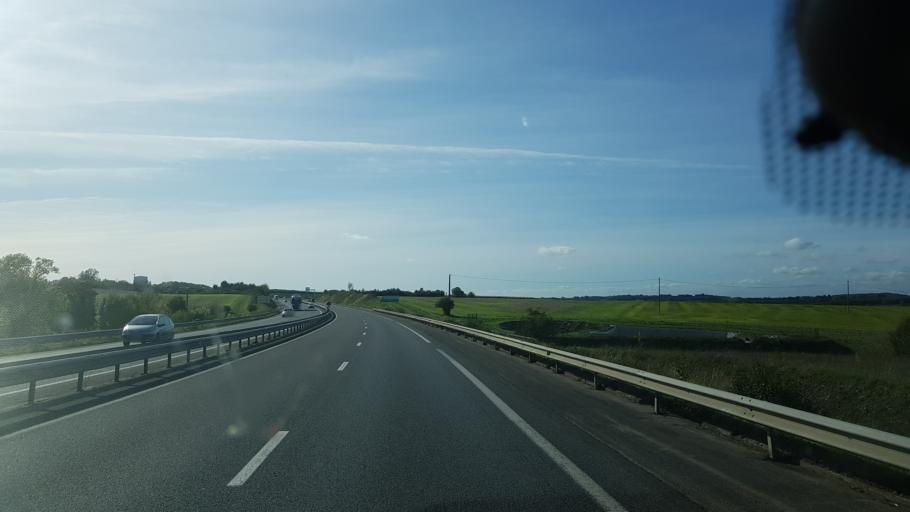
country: FR
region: Poitou-Charentes
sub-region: Departement de la Charente
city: Mornac
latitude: 45.7084
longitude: 0.2767
